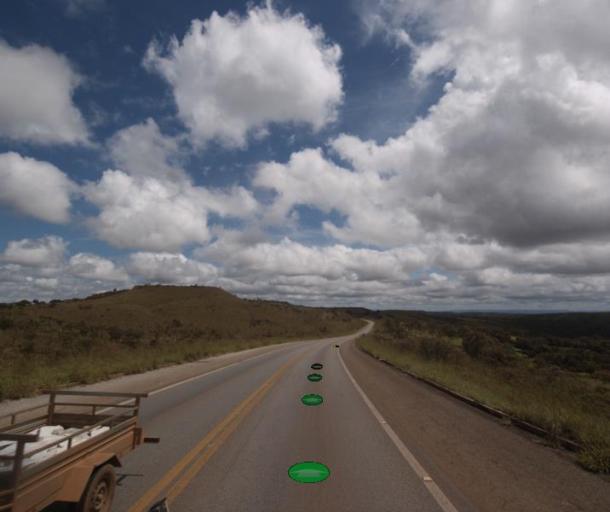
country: BR
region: Federal District
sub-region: Brasilia
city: Brasilia
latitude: -15.7540
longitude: -48.4178
